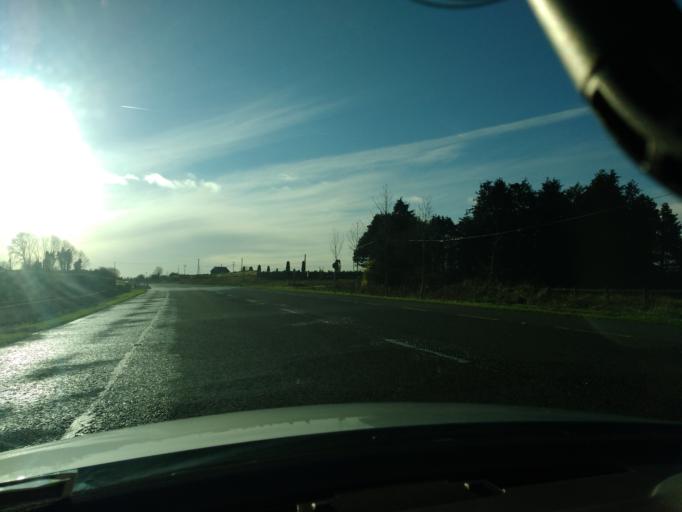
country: IE
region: Munster
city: Thurles
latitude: 52.6853
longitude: -7.6657
